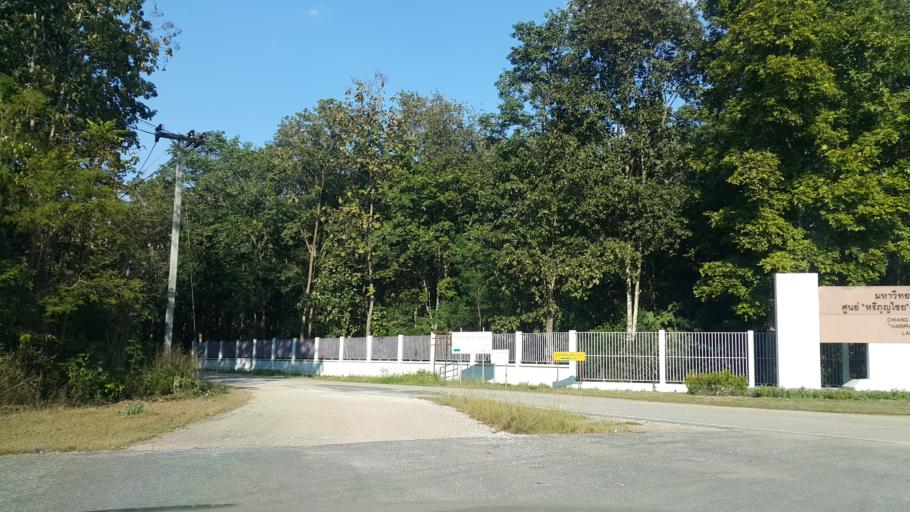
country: TH
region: Lamphun
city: Mae Tha
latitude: 18.5118
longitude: 99.1104
